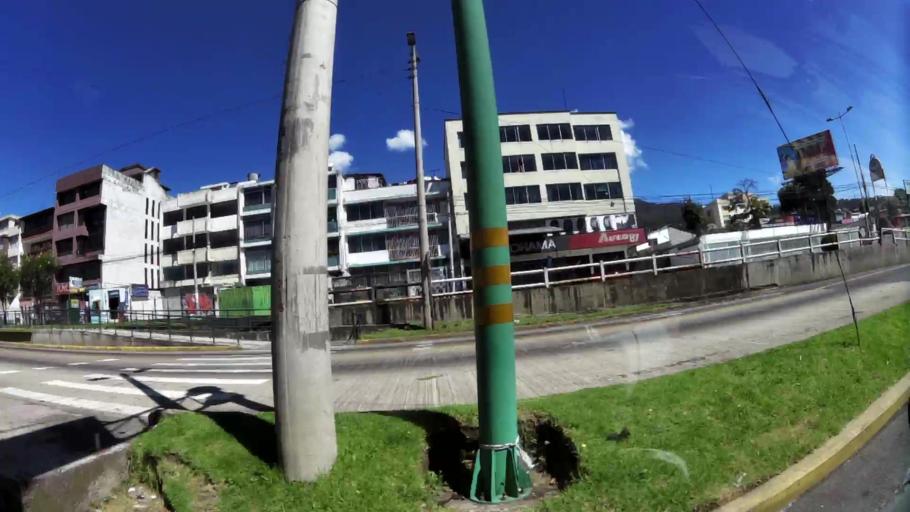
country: EC
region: Pichincha
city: Quito
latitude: -0.1782
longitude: -78.4940
